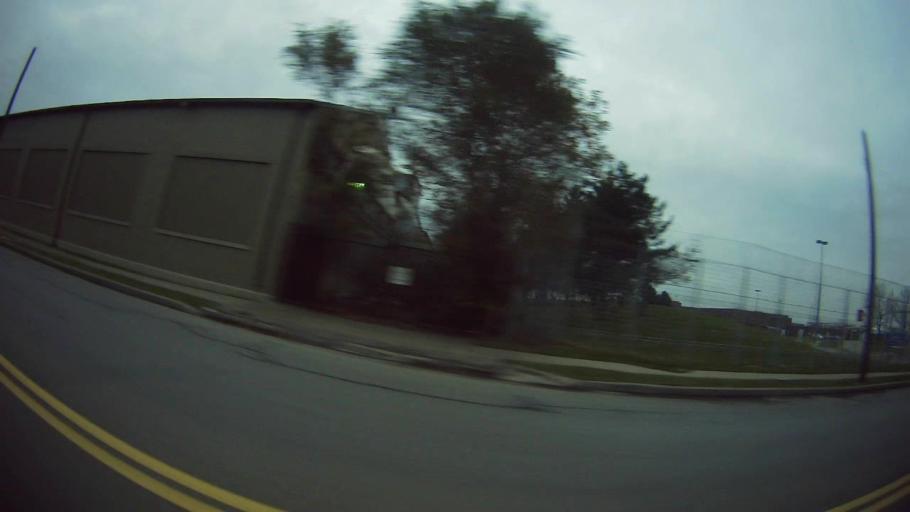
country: US
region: Michigan
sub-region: Wayne County
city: Hamtramck
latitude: 42.4250
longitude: -83.0627
